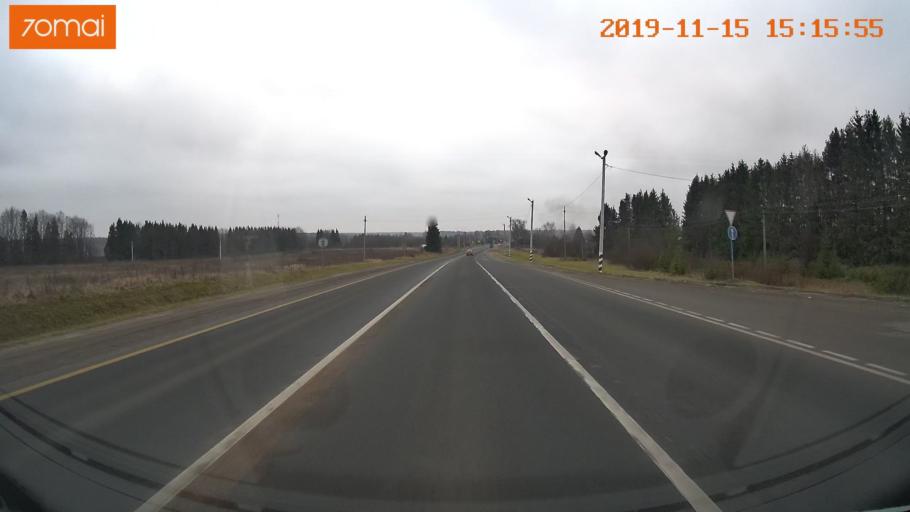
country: RU
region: Jaroslavl
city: Danilov
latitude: 58.2782
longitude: 40.1960
